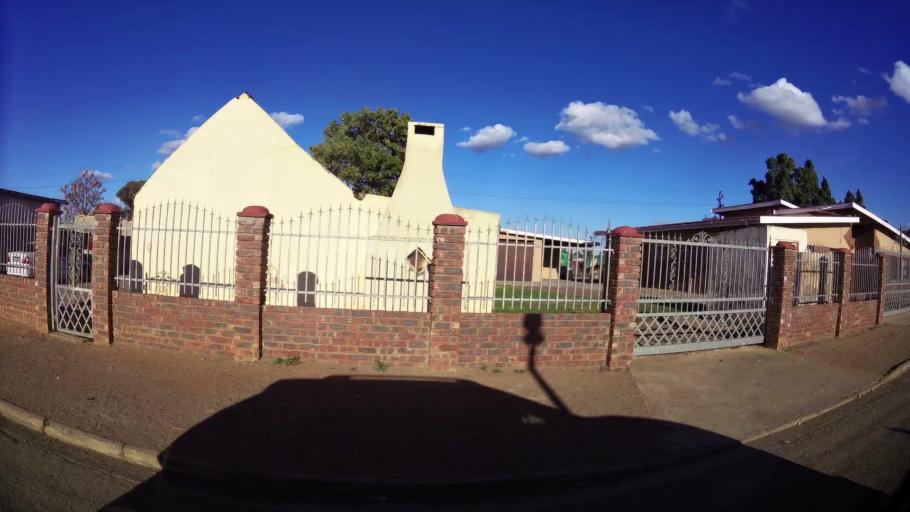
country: ZA
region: Western Cape
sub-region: Eden District Municipality
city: Riversdale
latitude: -34.1000
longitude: 20.9617
